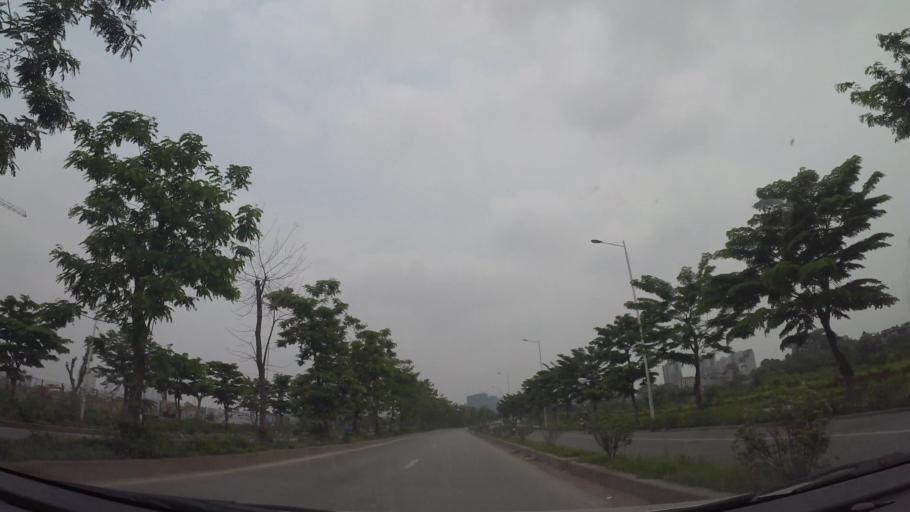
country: VN
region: Ha Noi
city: Cau Dien
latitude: 21.0371
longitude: 105.7482
